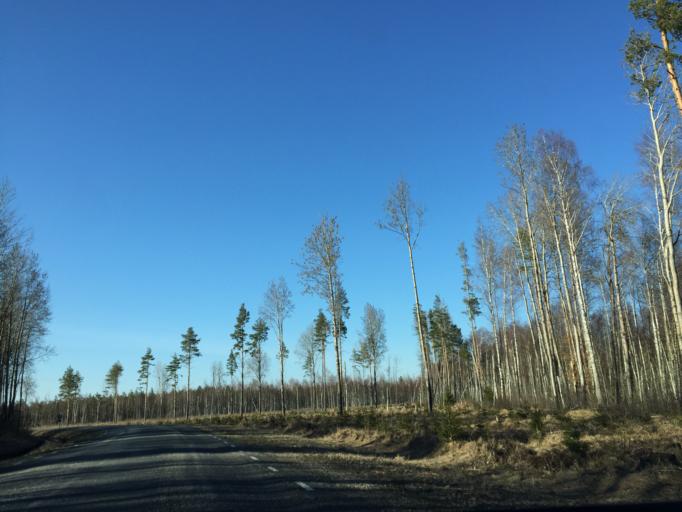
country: RU
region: Pskov
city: Gdov
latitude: 59.0075
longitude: 27.6866
